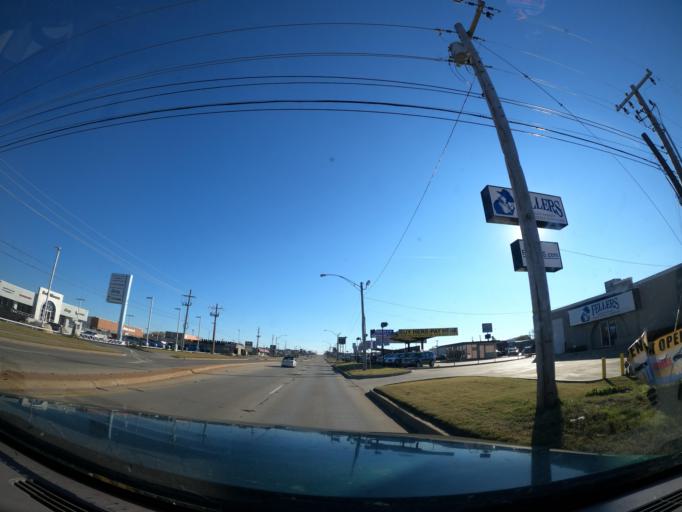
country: US
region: Oklahoma
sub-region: Tulsa County
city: Broken Arrow
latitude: 36.0972
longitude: -95.8867
